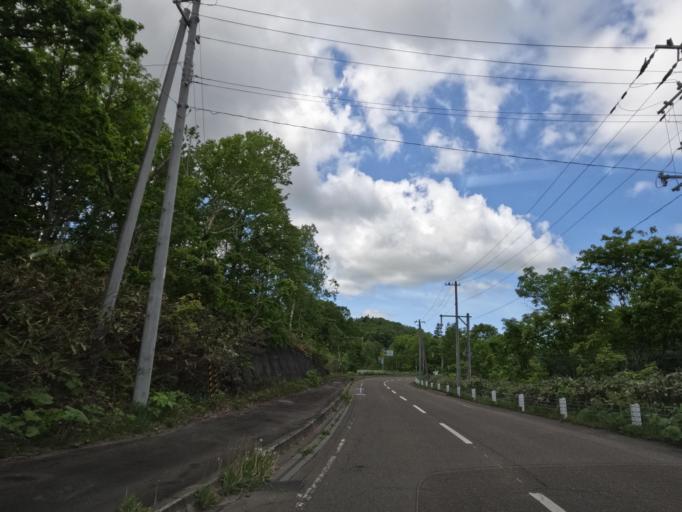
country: JP
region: Hokkaido
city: Tobetsu
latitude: 43.4729
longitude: 141.5955
